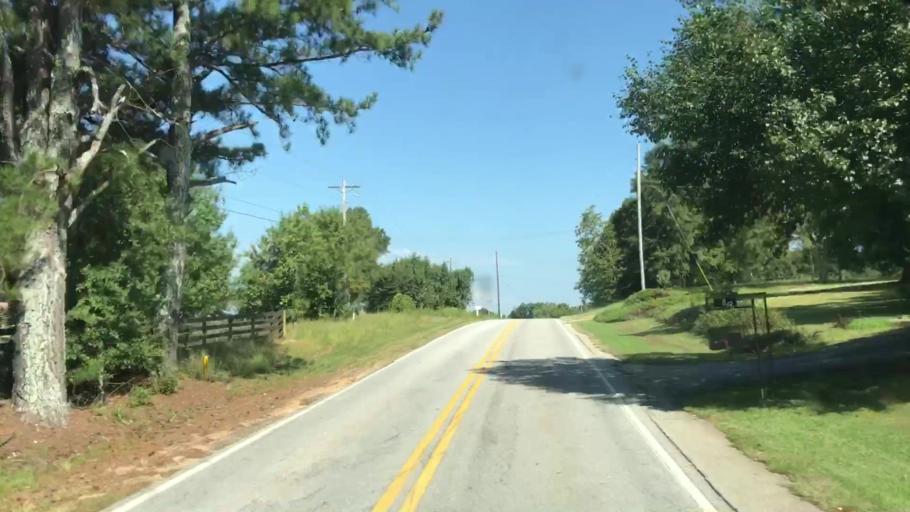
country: US
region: Georgia
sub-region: Walton County
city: Loganville
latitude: 33.8420
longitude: -83.8551
